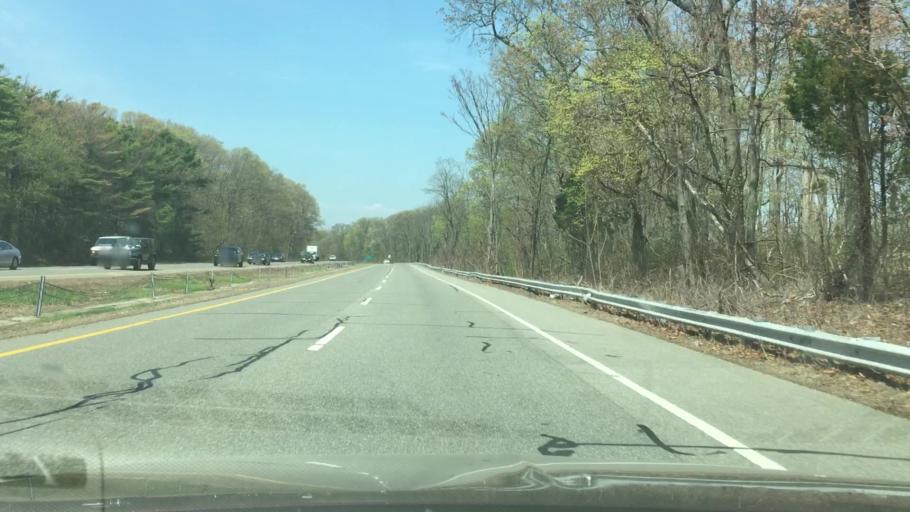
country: US
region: New York
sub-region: Suffolk County
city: Setauket-East Setauket
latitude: 40.9186
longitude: -73.1158
